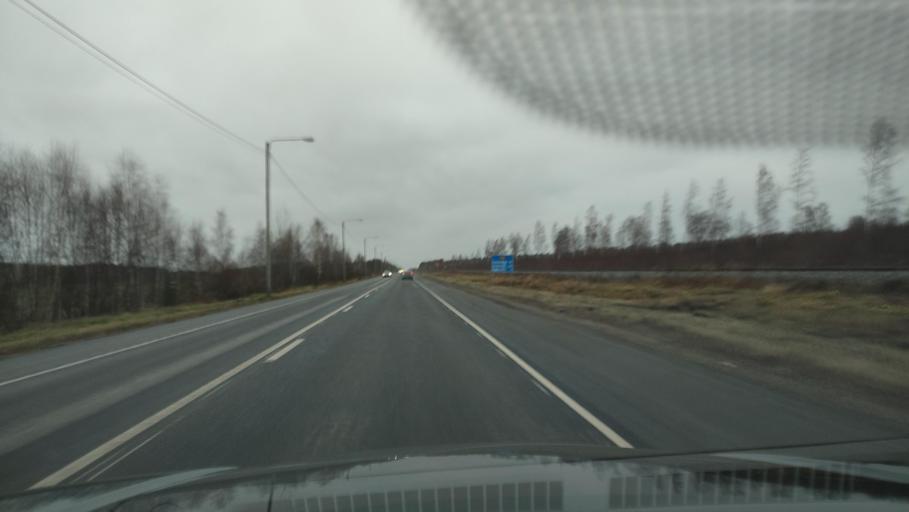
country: FI
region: Southern Ostrobothnia
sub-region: Seinaejoki
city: Ilmajoki
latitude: 62.7560
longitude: 22.6601
